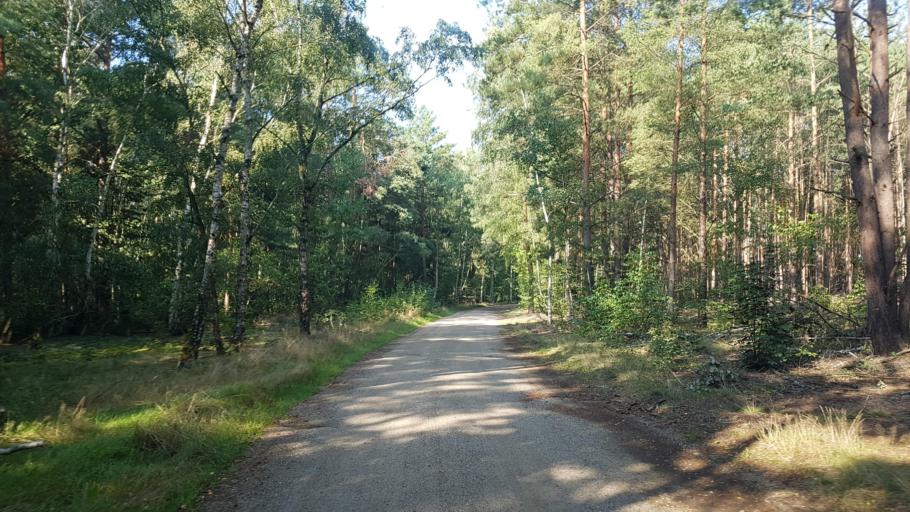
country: DE
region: Brandenburg
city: Luckau
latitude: 51.7861
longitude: 13.6930
